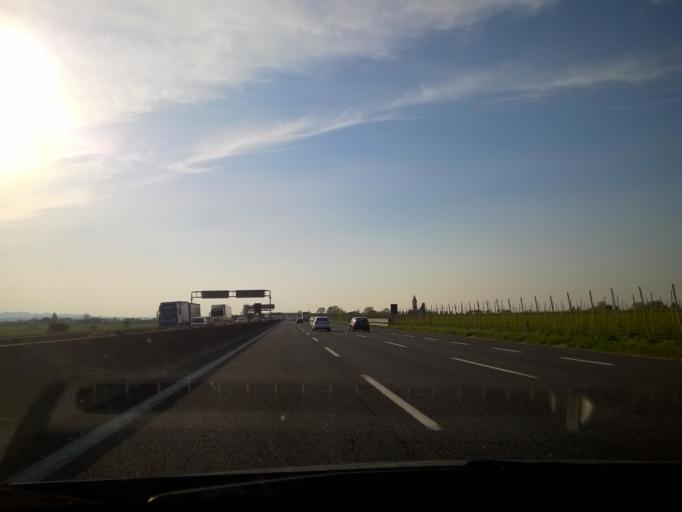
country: IT
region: Emilia-Romagna
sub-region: Provincia di Ravenna
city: Castel Bolognese
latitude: 44.3567
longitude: 11.8068
